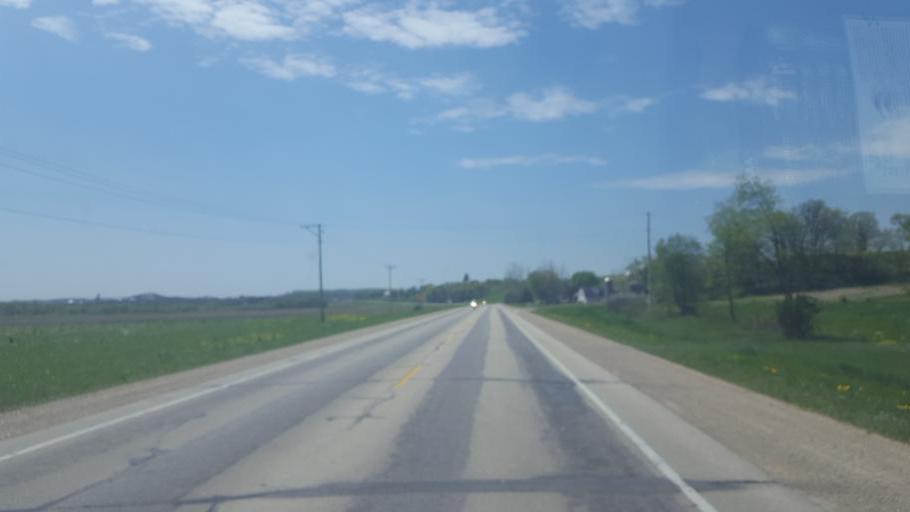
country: US
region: Wisconsin
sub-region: Vernon County
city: Hillsboro
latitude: 43.6789
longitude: -90.2893
